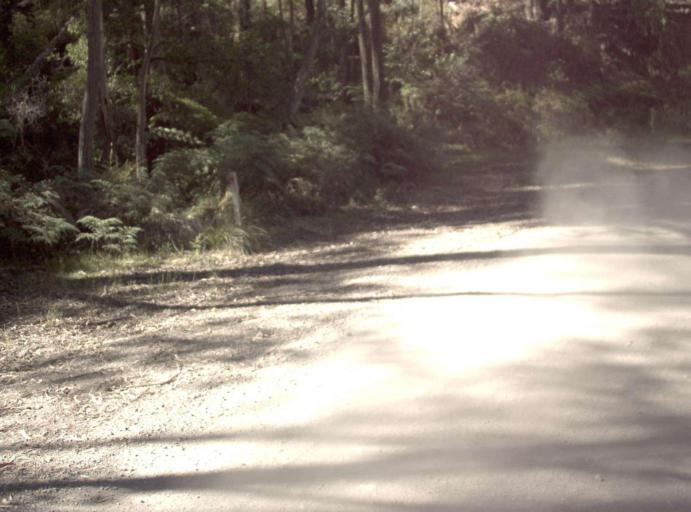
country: AU
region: New South Wales
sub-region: Bombala
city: Bombala
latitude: -37.2664
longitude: 148.7263
